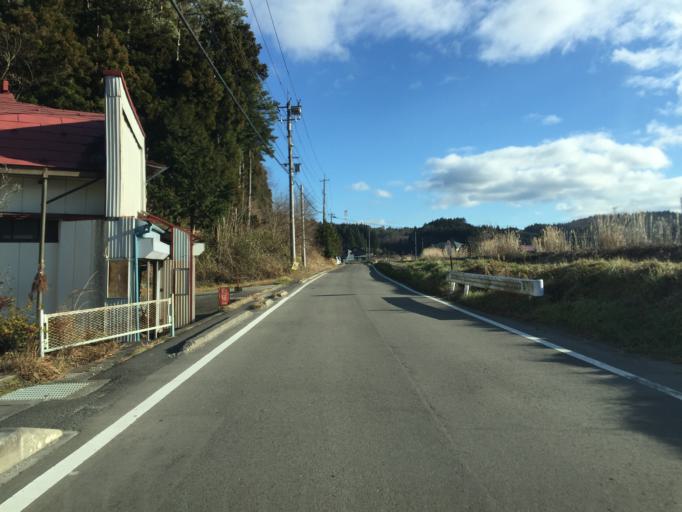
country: JP
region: Fukushima
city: Funehikimachi-funehiki
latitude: 37.2511
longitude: 140.6660
